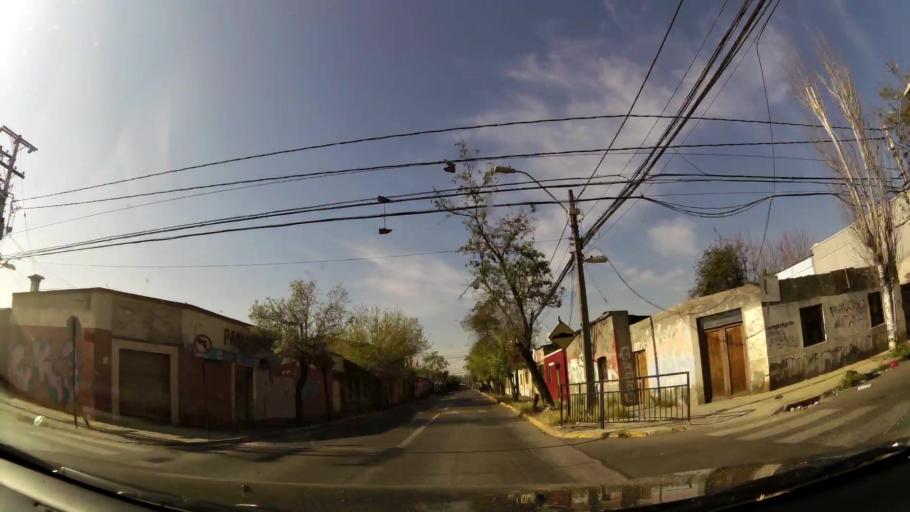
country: CL
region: Santiago Metropolitan
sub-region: Provincia de Santiago
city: Santiago
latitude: -33.4020
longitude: -70.6761
